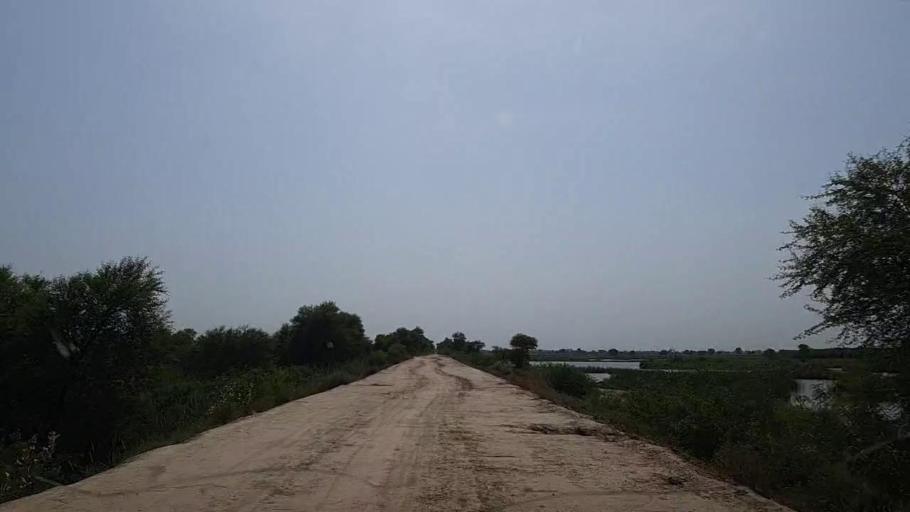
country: PK
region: Sindh
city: Ghotki
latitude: 28.0840
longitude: 69.4024
